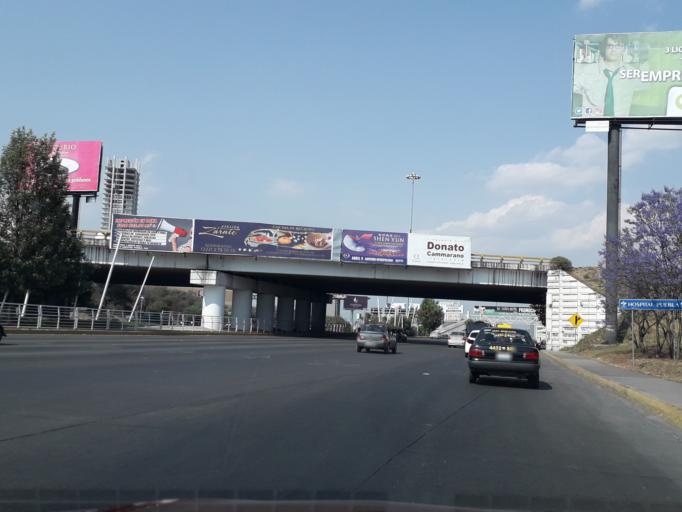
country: MX
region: Puebla
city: Puebla
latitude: 19.0283
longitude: -98.2330
